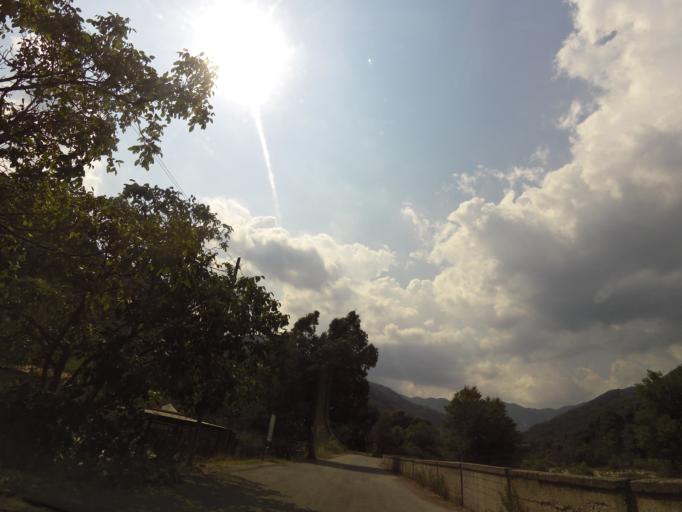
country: IT
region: Calabria
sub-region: Provincia di Reggio Calabria
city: Bivongi
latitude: 38.4836
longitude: 16.4429
